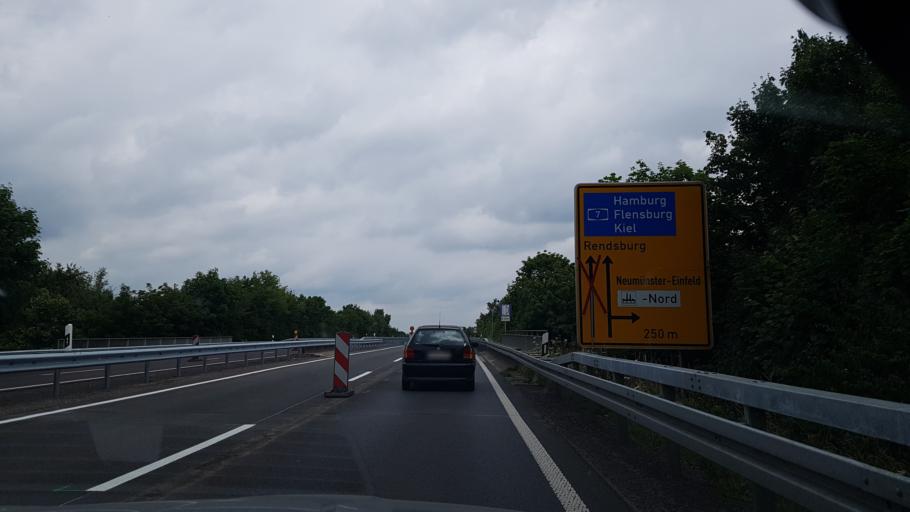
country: DE
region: Schleswig-Holstein
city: Neumunster
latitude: 54.0964
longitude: 9.9740
